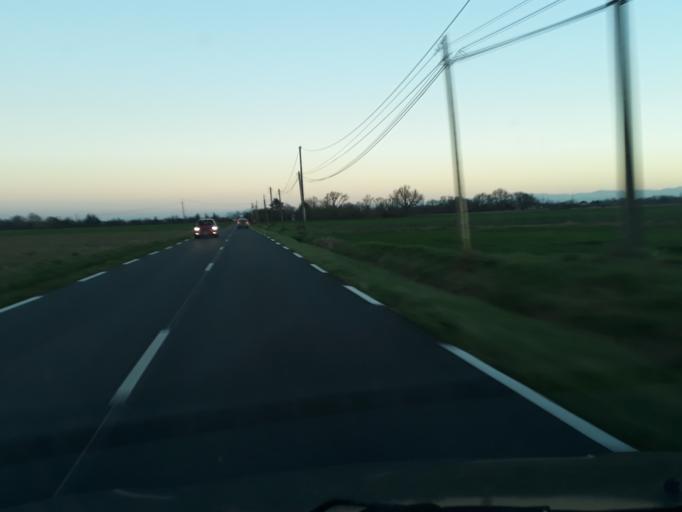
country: FR
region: Midi-Pyrenees
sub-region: Departement de la Haute-Garonne
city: Saint-Lys
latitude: 43.5356
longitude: 1.1664
